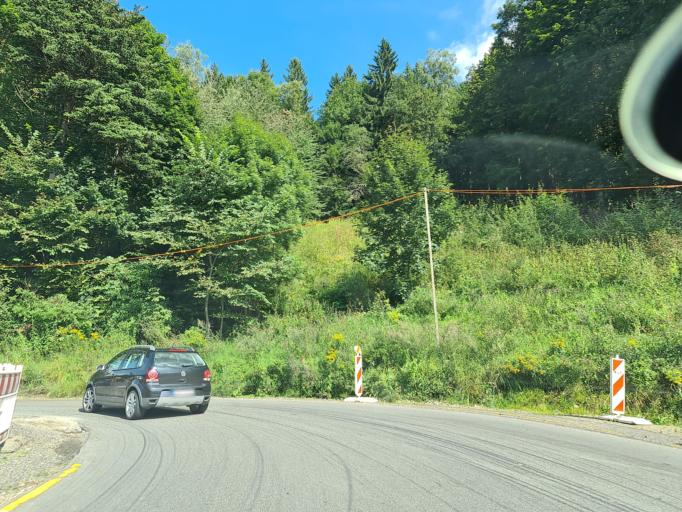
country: DE
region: Saxony
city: Pobershau
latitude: 50.6565
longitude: 13.2118
